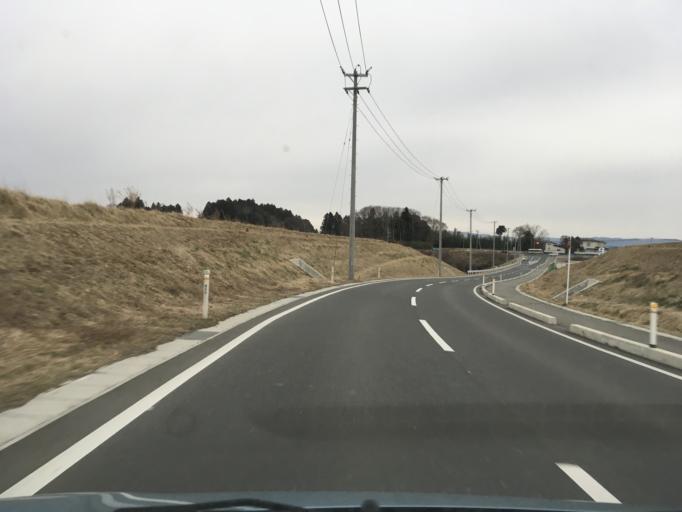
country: JP
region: Miyagi
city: Wakuya
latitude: 38.6951
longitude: 141.1711
